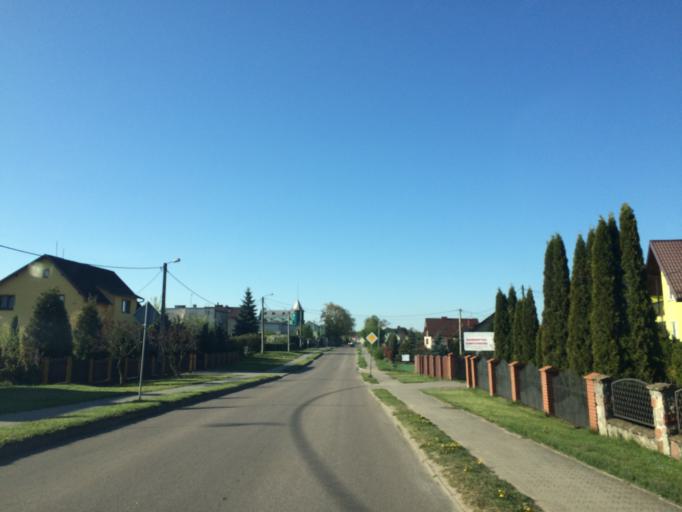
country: PL
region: Warmian-Masurian Voivodeship
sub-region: Powiat dzialdowski
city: Rybno
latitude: 53.3915
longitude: 19.9320
